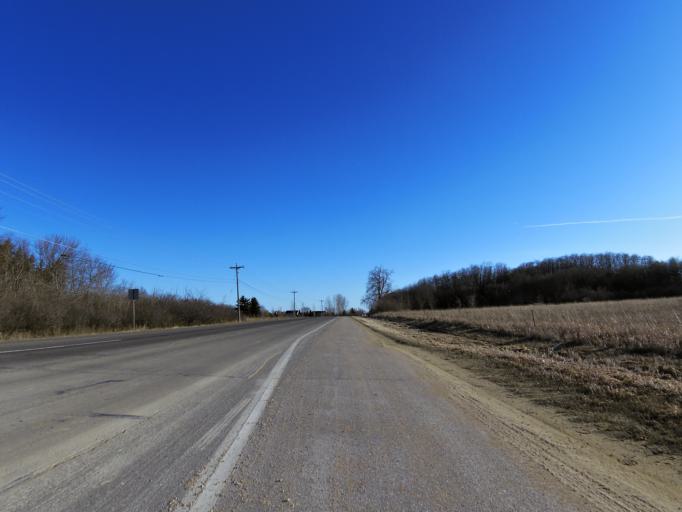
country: US
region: Minnesota
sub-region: Washington County
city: Bayport
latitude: 44.9891
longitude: -92.7905
